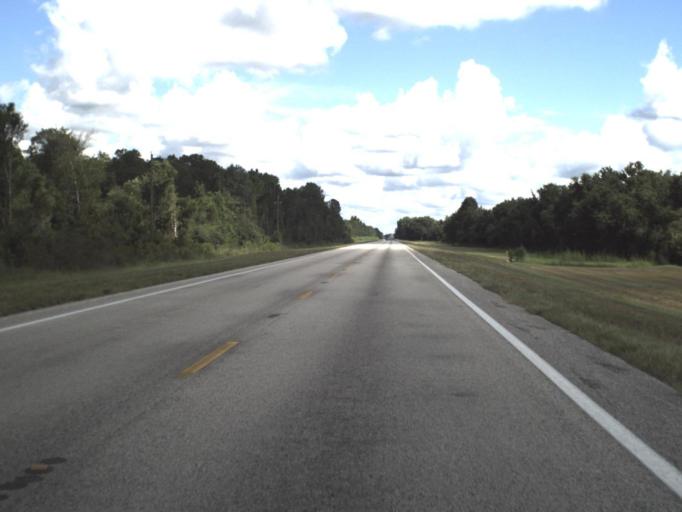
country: US
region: Florida
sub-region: Pasco County
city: Zephyrhills North
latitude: 28.2636
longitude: -82.0555
